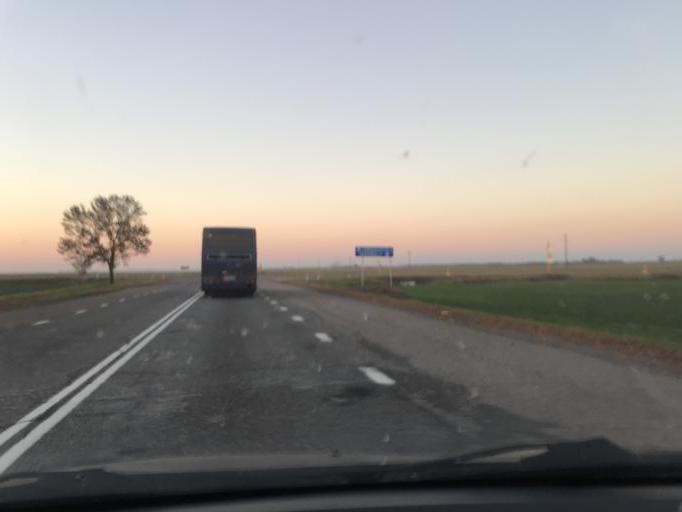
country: BY
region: Gomel
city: Horad Rechytsa
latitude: 52.2221
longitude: 30.5194
